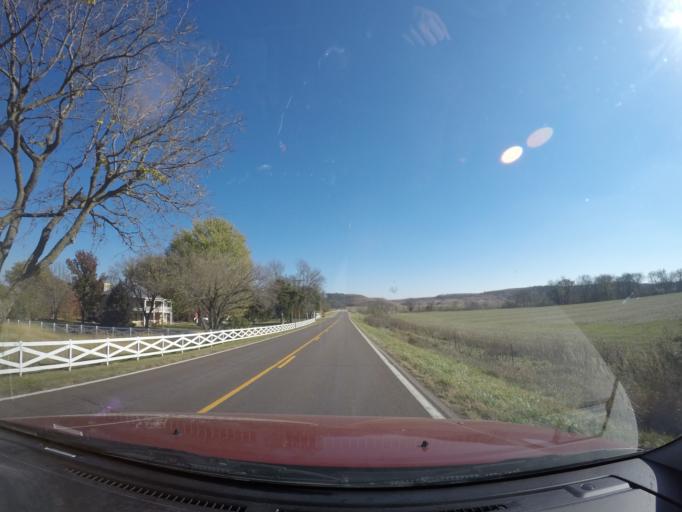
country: US
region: Kansas
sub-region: Geary County
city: Grandview Plaza
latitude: 39.0080
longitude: -96.7424
